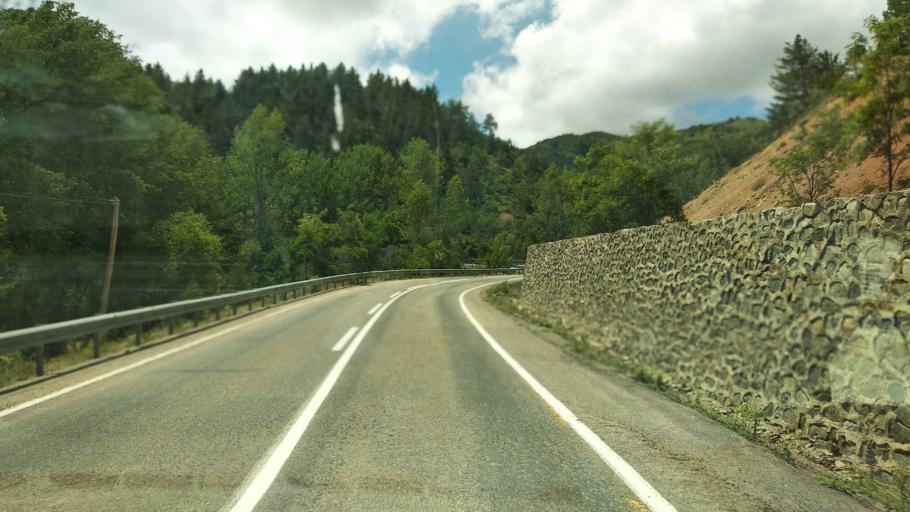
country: TR
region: Gumushane
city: Kose
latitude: 40.3018
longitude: 39.5557
